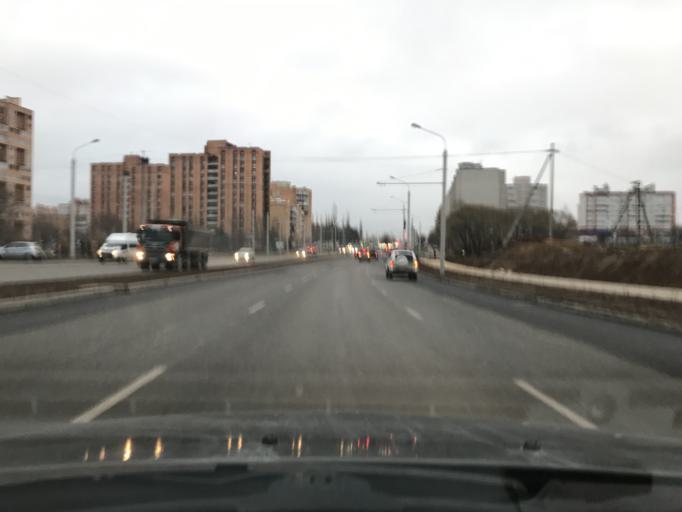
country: RU
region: Kaluga
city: Kaluga
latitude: 54.4911
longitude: 36.2104
